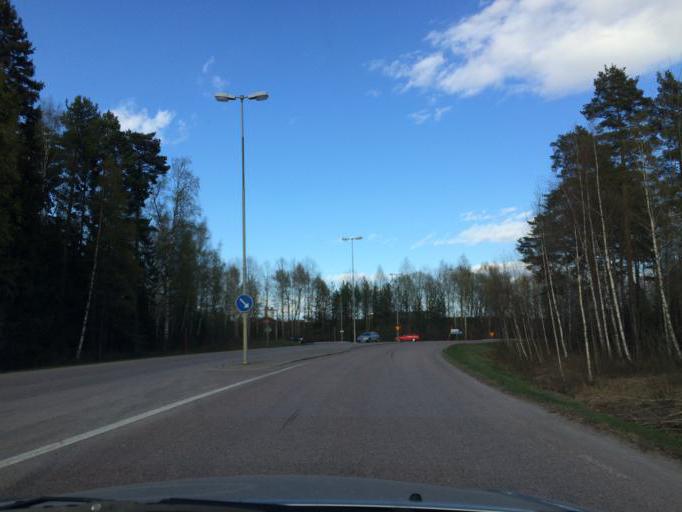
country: SE
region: Vaestmanland
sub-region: Vasteras
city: Hokasen
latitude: 59.6481
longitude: 16.5582
